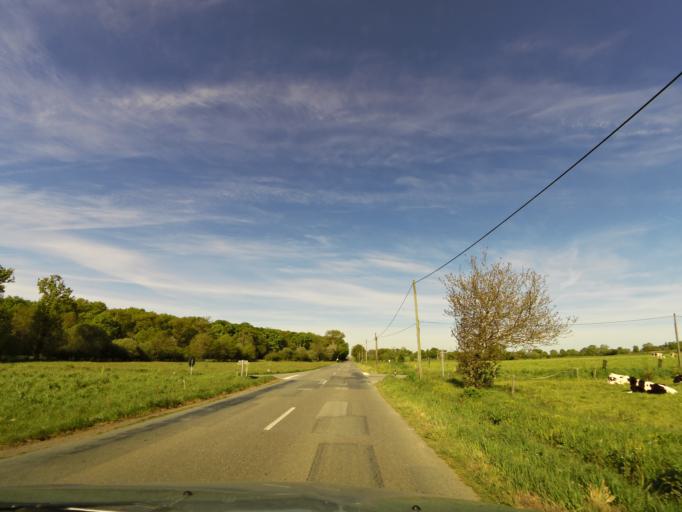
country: FR
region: Brittany
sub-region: Departement d'Ille-et-Vilaine
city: Pance
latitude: 47.8723
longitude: -1.6228
